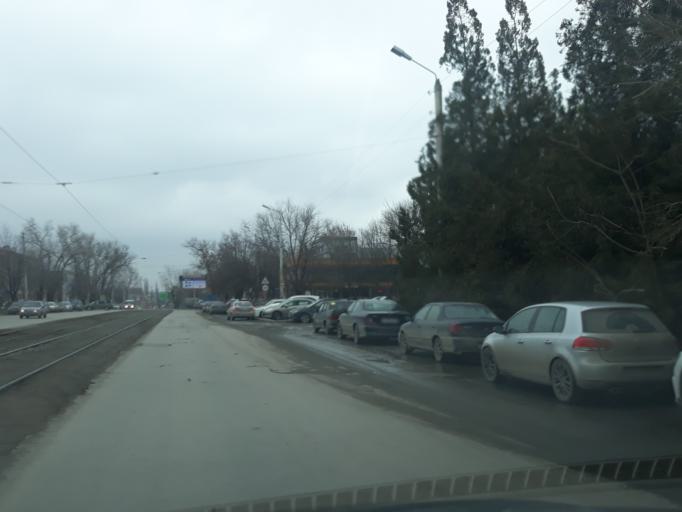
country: RU
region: Rostov
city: Taganrog
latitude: 47.2429
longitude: 38.8905
